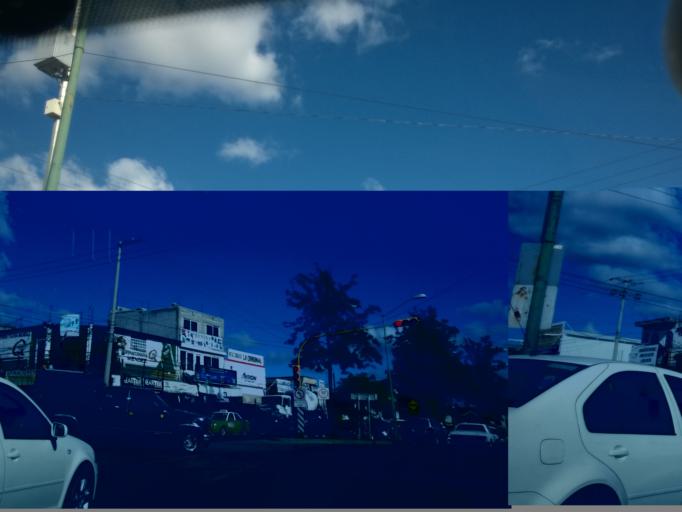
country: MX
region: Guanajuato
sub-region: Leon
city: Ejido la Joya
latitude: 21.1194
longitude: -101.7170
